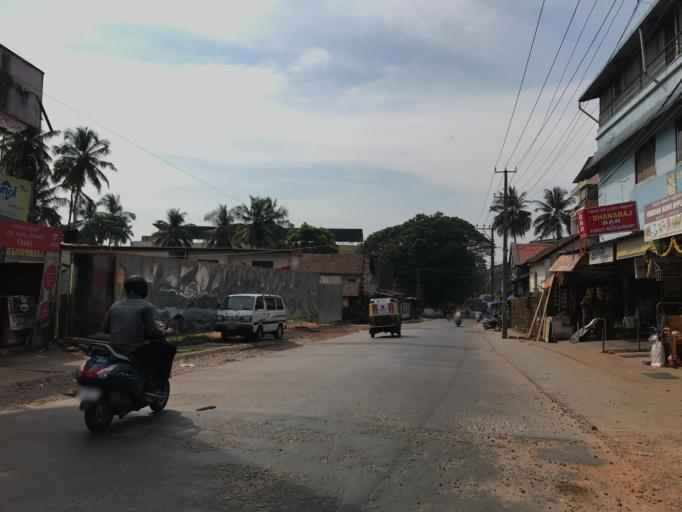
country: IN
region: Karnataka
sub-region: Dakshina Kannada
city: Ullal
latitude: 12.8483
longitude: 74.8524
